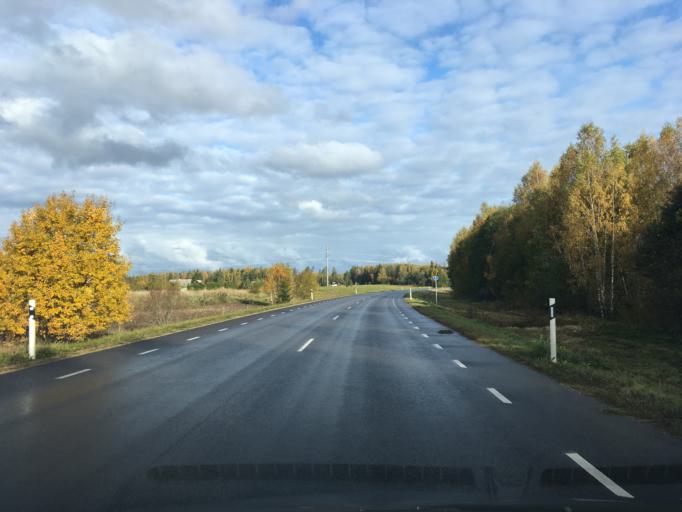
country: EE
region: Harju
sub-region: Raasiku vald
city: Raasiku
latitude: 59.2020
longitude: 25.1832
